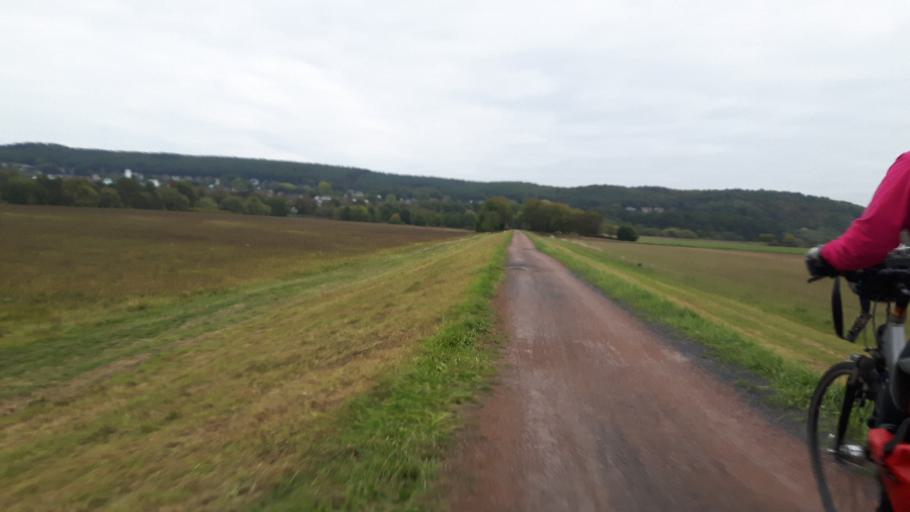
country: DE
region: North Rhine-Westphalia
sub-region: Regierungsbezirk Koln
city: Stossdorf
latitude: 50.7936
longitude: 7.2529
